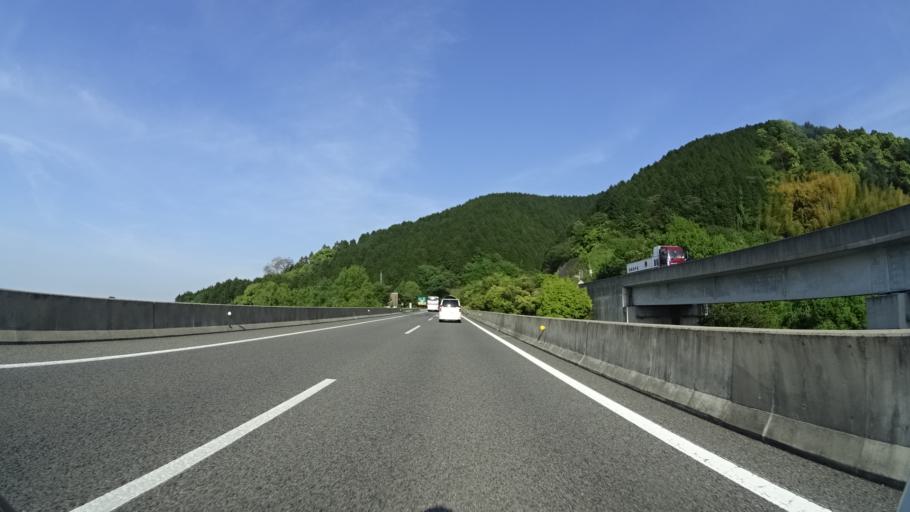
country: JP
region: Ehime
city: Saijo
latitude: 33.8862
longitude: 133.1448
